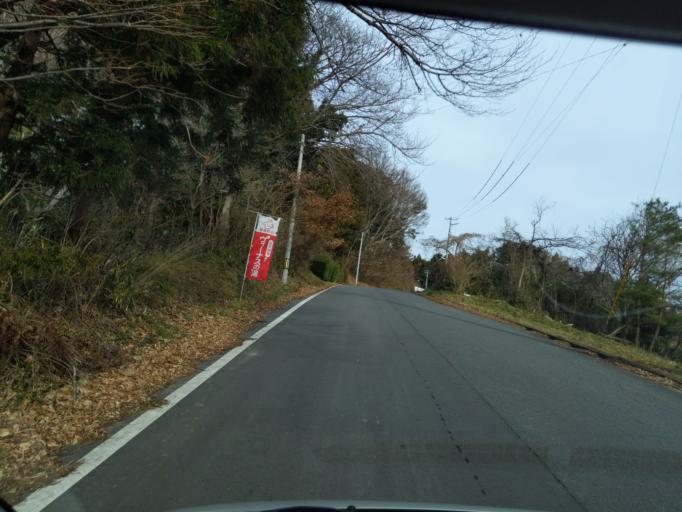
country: JP
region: Miyagi
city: Wakuya
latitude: 38.6944
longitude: 141.1441
